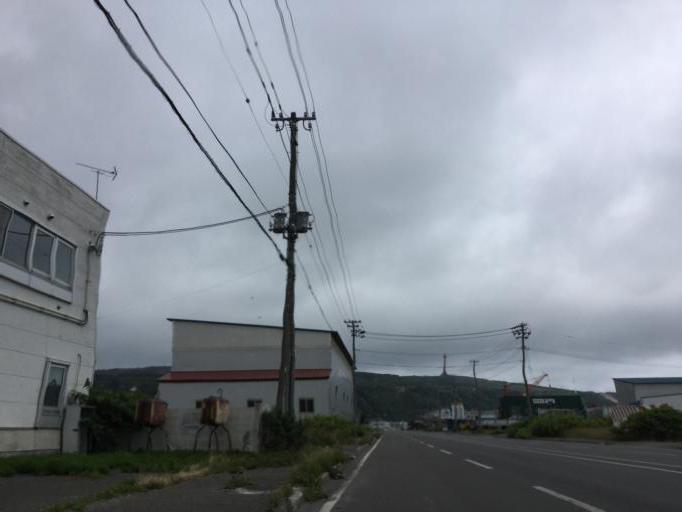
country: JP
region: Hokkaido
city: Wakkanai
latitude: 45.4026
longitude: 141.6851
